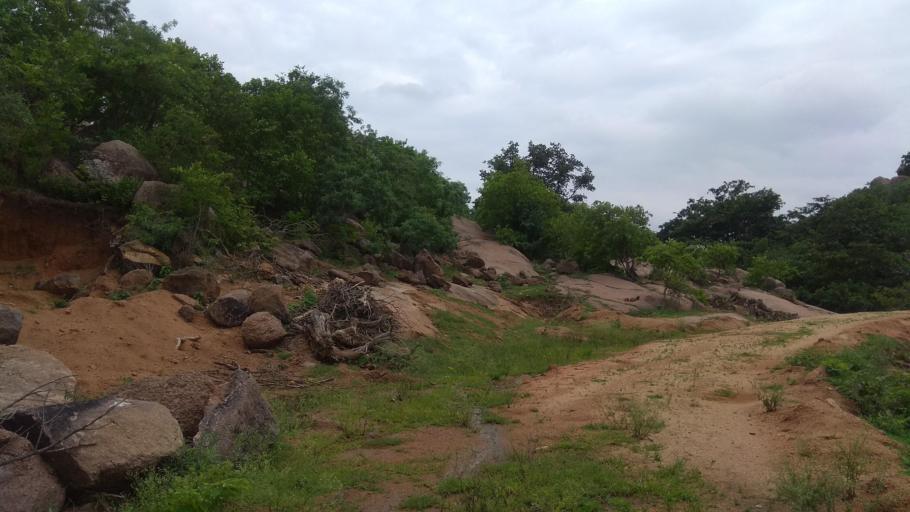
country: IN
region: Telangana
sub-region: Mahbubnagar
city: Farrukhnagar
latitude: 16.8940
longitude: 78.5005
